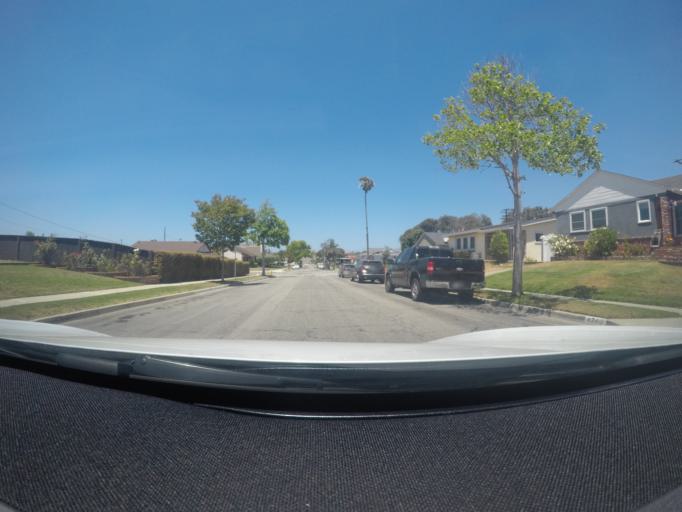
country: US
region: California
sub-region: Los Angeles County
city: Torrance
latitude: 33.8531
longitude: -118.3598
